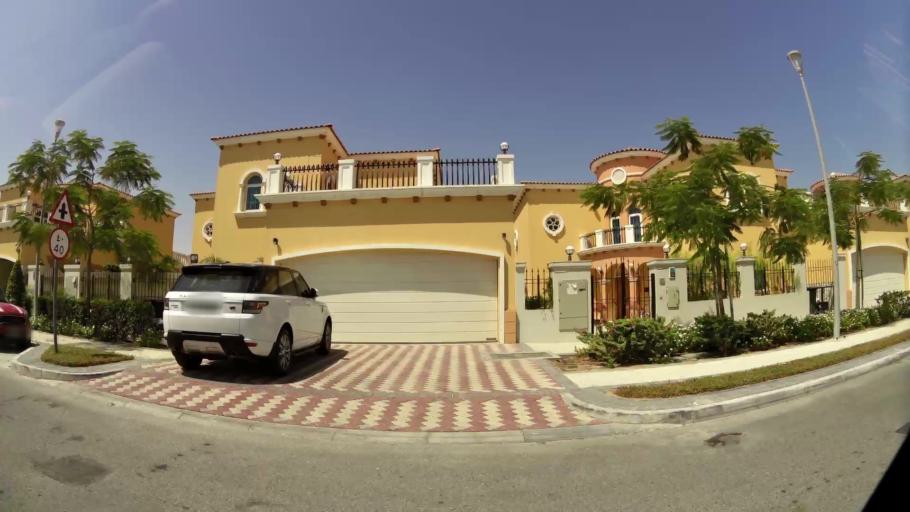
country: AE
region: Dubai
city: Dubai
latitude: 25.0544
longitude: 55.1469
